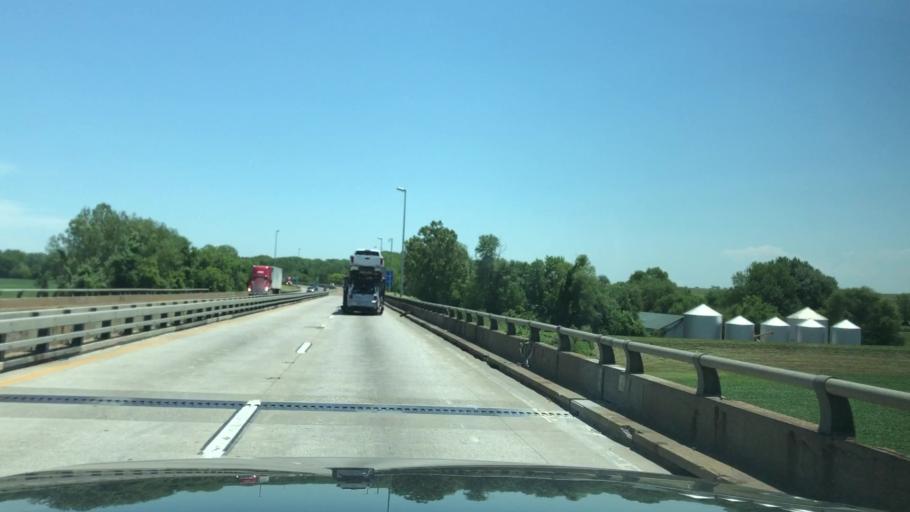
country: US
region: Missouri
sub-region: Saint Louis County
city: Glasgow Village
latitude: 38.7622
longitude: -90.1638
